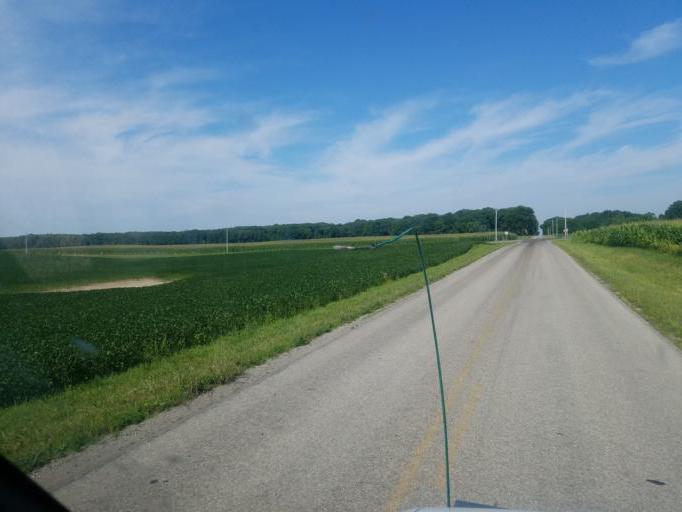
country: US
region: Ohio
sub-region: Hardin County
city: Kenton
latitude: 40.5552
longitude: -83.6374
